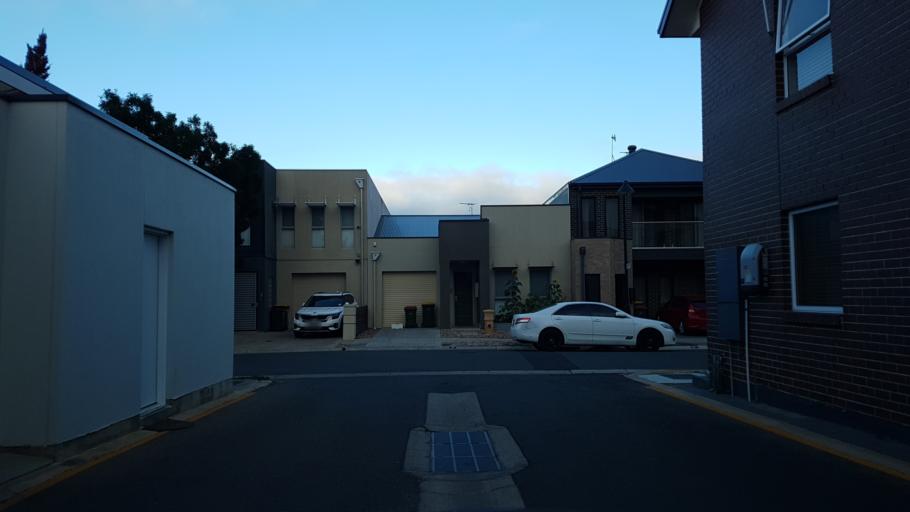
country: AU
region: South Australia
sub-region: Salisbury
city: Ingle Farm
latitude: -34.8065
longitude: 138.6114
